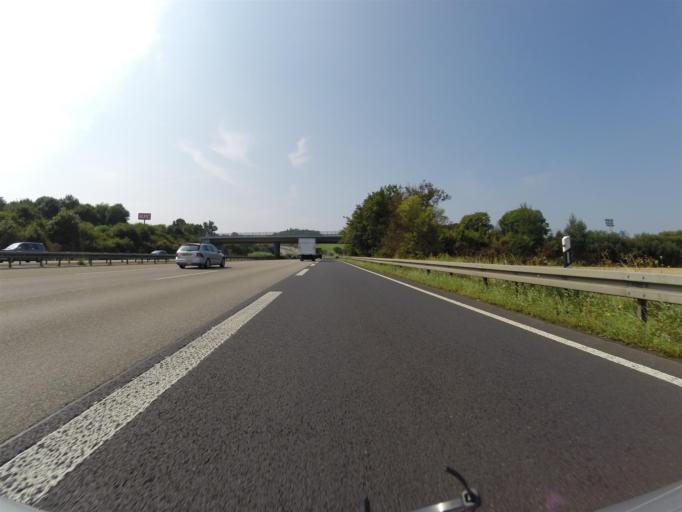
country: DE
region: Hesse
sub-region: Regierungsbezirk Kassel
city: Guxhagen
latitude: 51.2066
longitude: 9.4687
